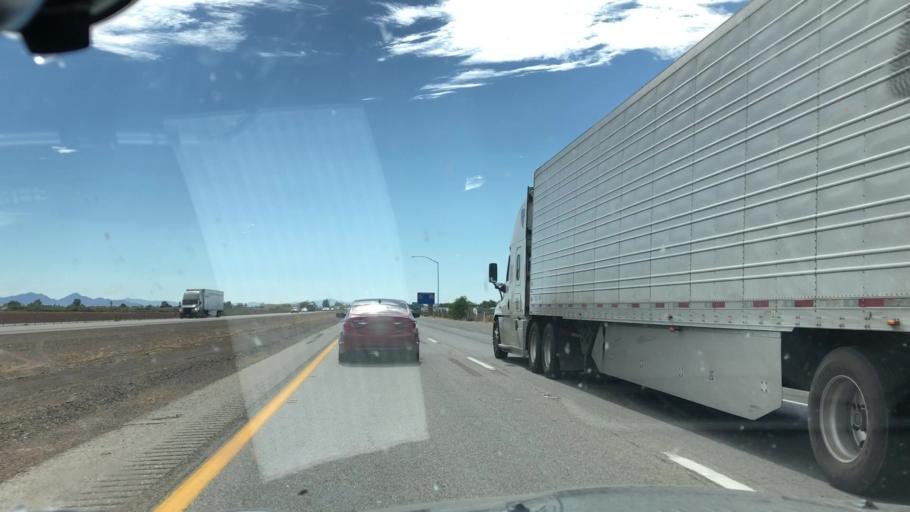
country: US
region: Arizona
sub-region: La Paz County
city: Ehrenberg
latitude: 33.6079
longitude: -114.5520
